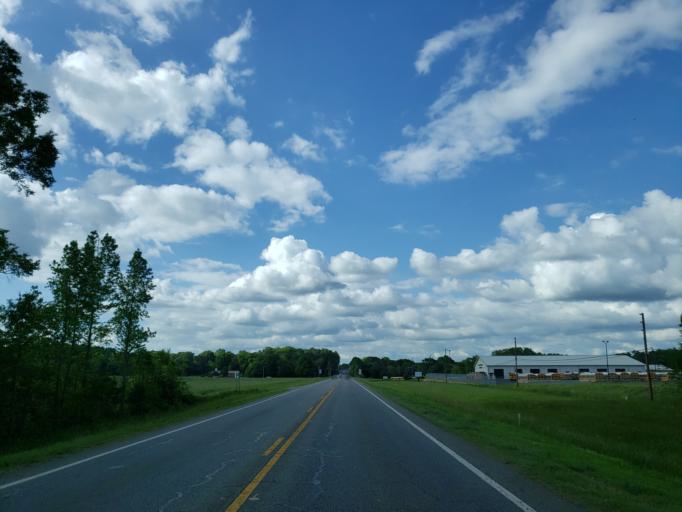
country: US
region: Georgia
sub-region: Bartow County
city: Cartersville
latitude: 34.2398
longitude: -84.8568
